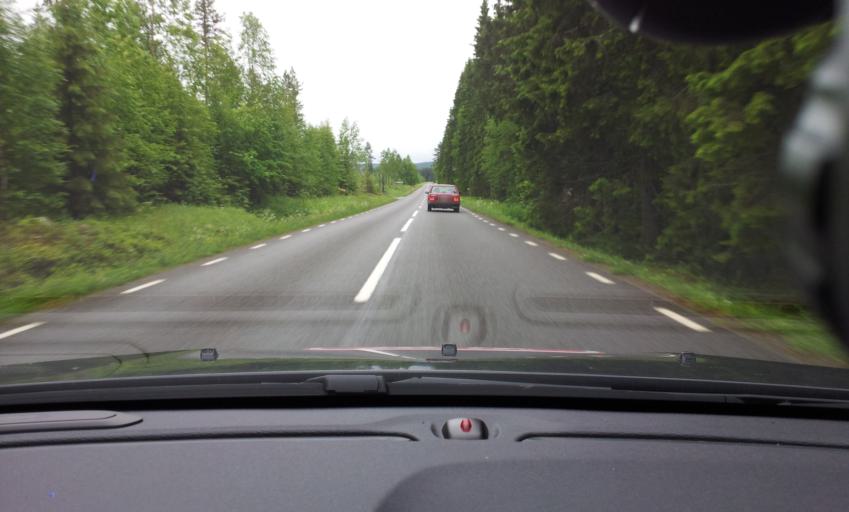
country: SE
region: Jaemtland
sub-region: Stroemsunds Kommun
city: Stroemsund
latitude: 63.4435
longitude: 15.4795
